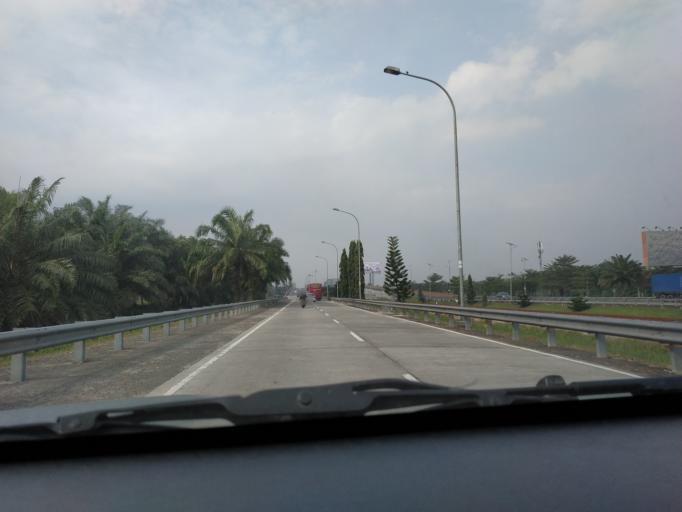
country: ID
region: North Sumatra
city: Percut
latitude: 3.6127
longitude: 98.8566
